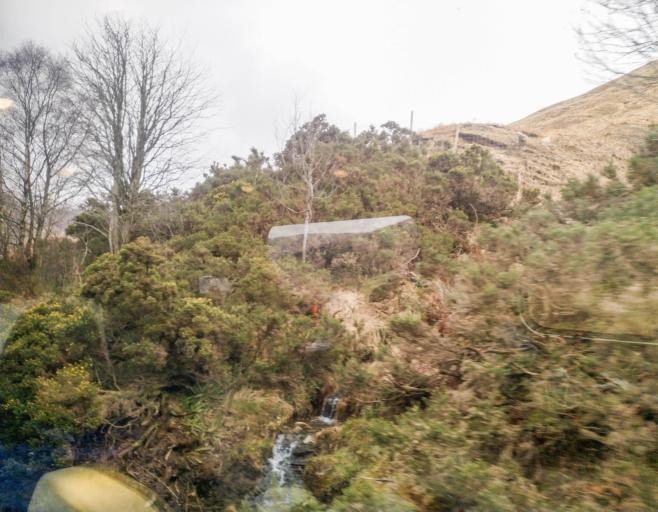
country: GB
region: Scotland
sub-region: Argyll and Bute
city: Garelochhead
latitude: 56.4735
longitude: -4.7176
